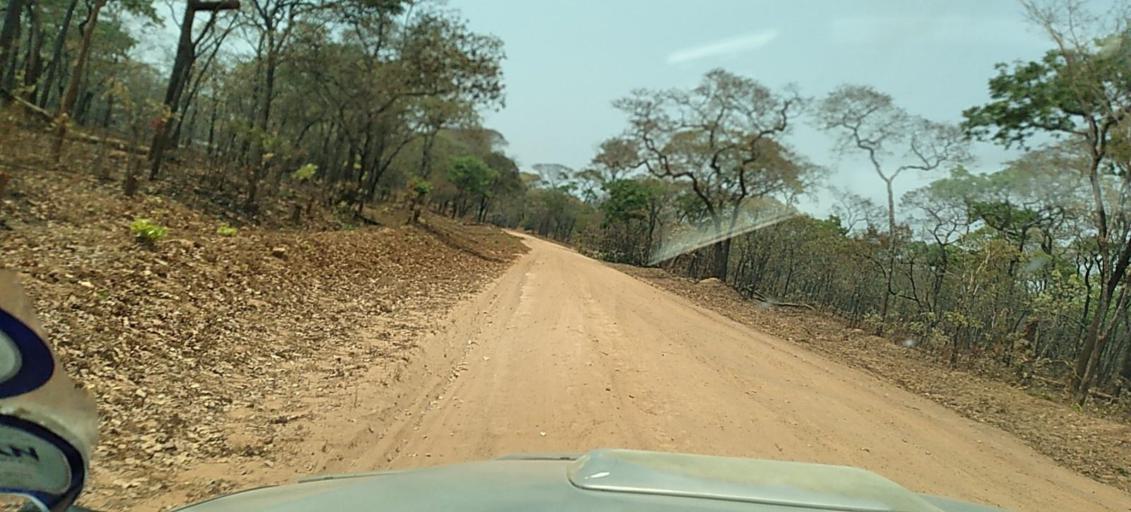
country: ZM
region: North-Western
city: Kasempa
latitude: -13.5478
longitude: 26.0525
